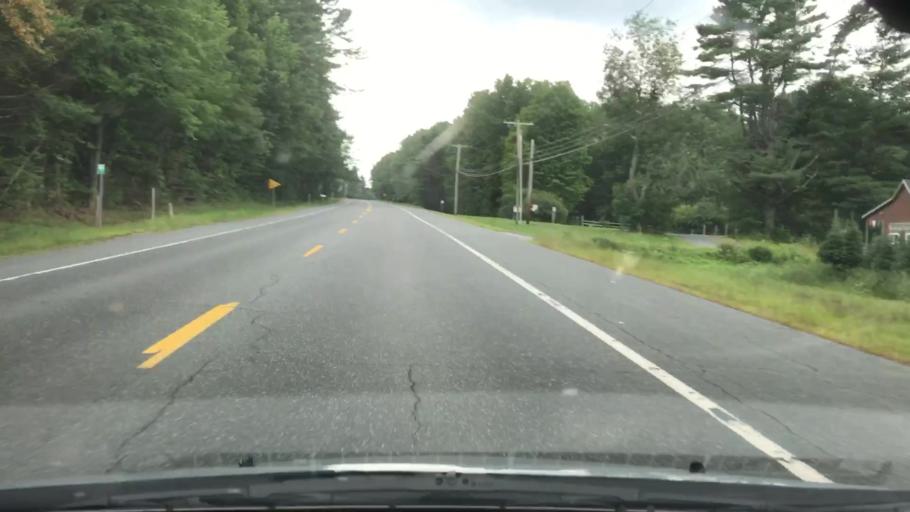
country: US
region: New Hampshire
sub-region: Grafton County
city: Lyme
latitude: 43.7875
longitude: -72.1750
